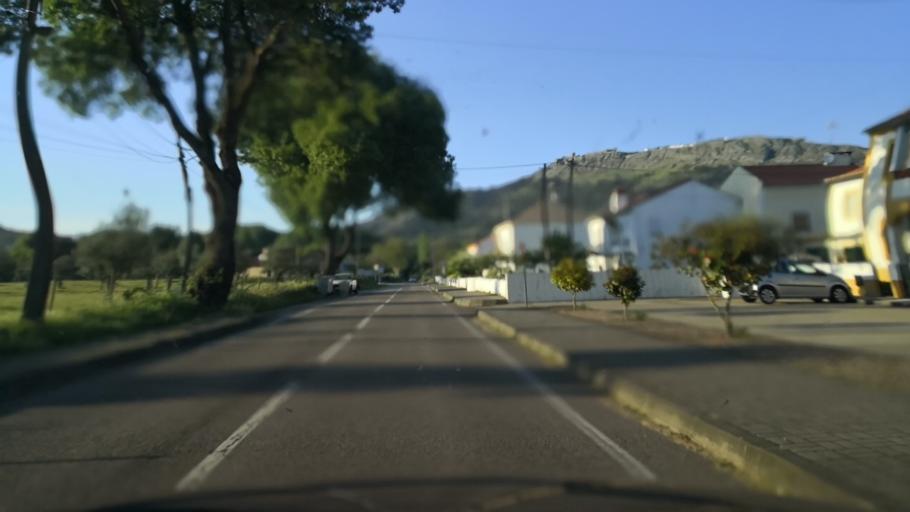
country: PT
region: Portalegre
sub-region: Marvao
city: Marvao
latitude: 39.3765
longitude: -7.3886
